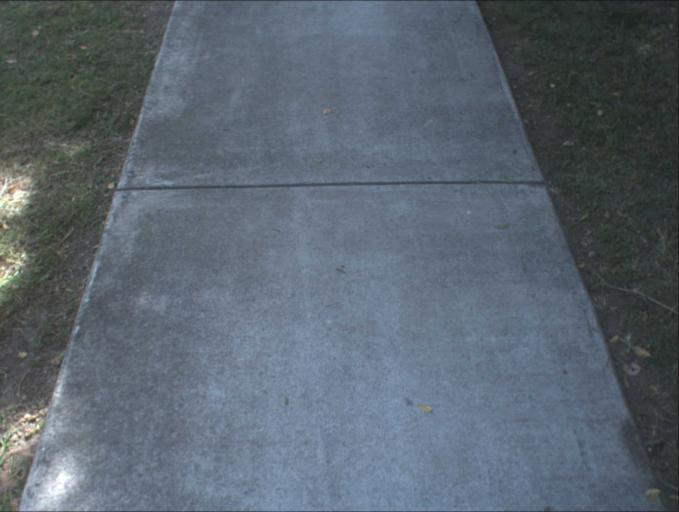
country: AU
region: Queensland
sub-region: Logan
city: Park Ridge South
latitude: -27.6776
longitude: 153.0547
